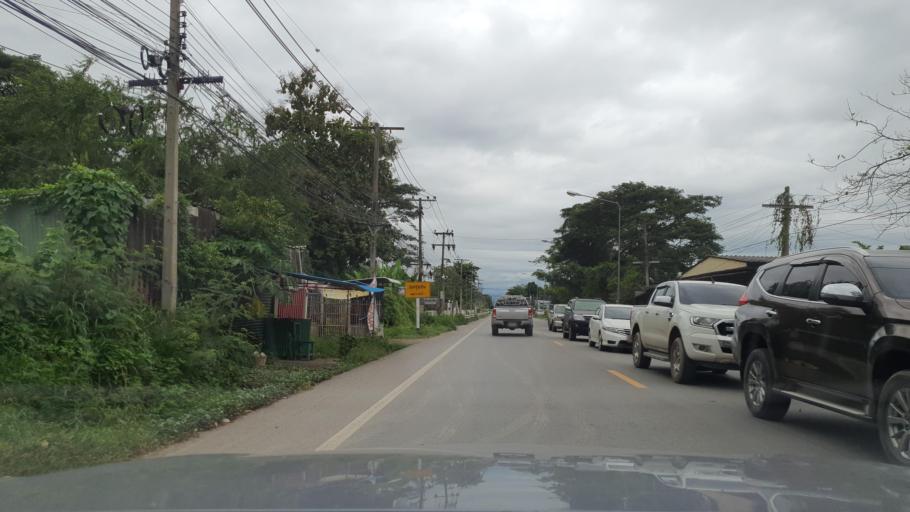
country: TH
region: Lamphun
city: Lamphun
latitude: 18.5847
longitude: 98.9917
